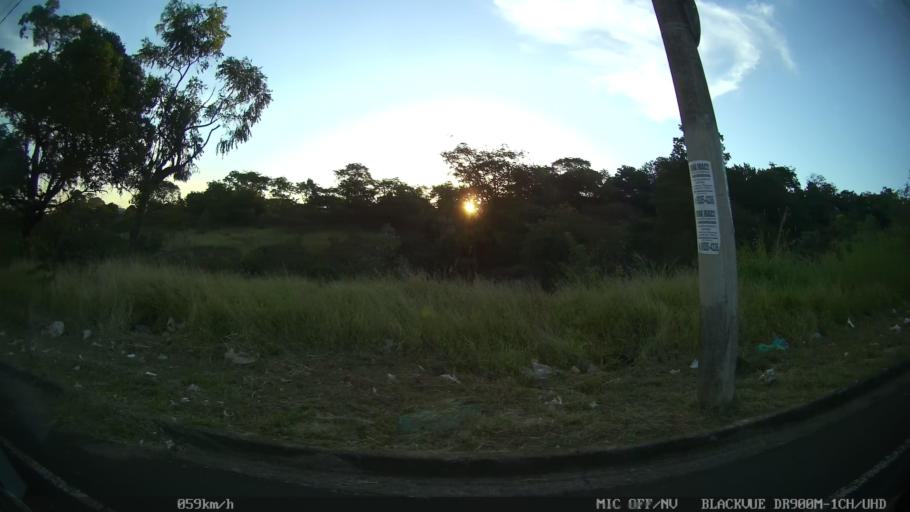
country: BR
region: Sao Paulo
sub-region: Franca
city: Franca
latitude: -20.5071
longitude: -47.4114
